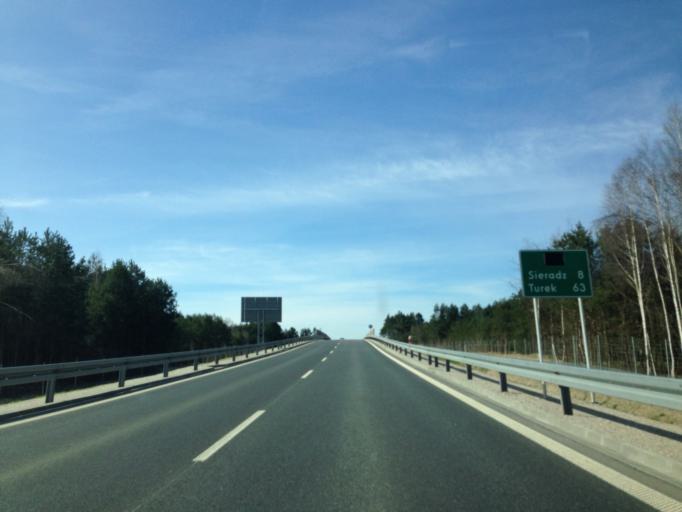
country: PL
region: Lodz Voivodeship
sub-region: Powiat zdunskowolski
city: Zapolice
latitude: 51.5989
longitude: 18.8178
